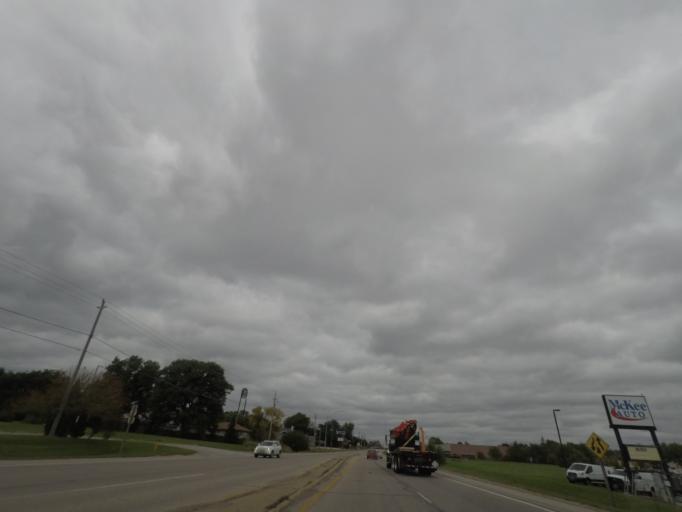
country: US
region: Iowa
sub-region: Polk County
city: Saylorville
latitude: 41.6533
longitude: -93.6004
